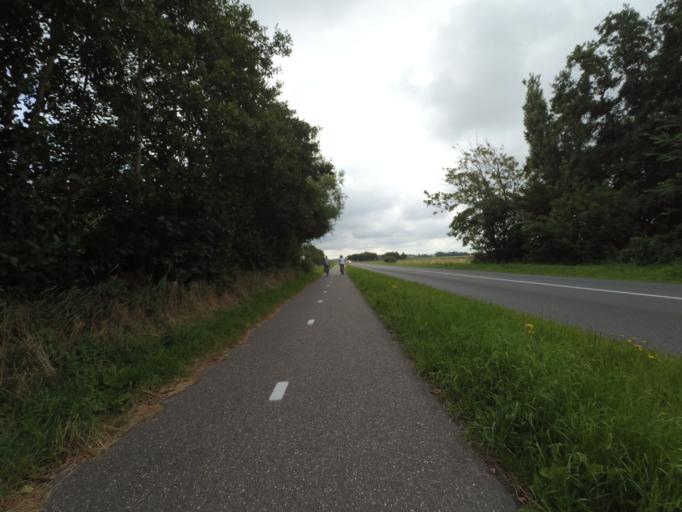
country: NL
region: North Holland
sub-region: Gemeente Texel
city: Den Burg
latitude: 53.0446
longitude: 4.8299
